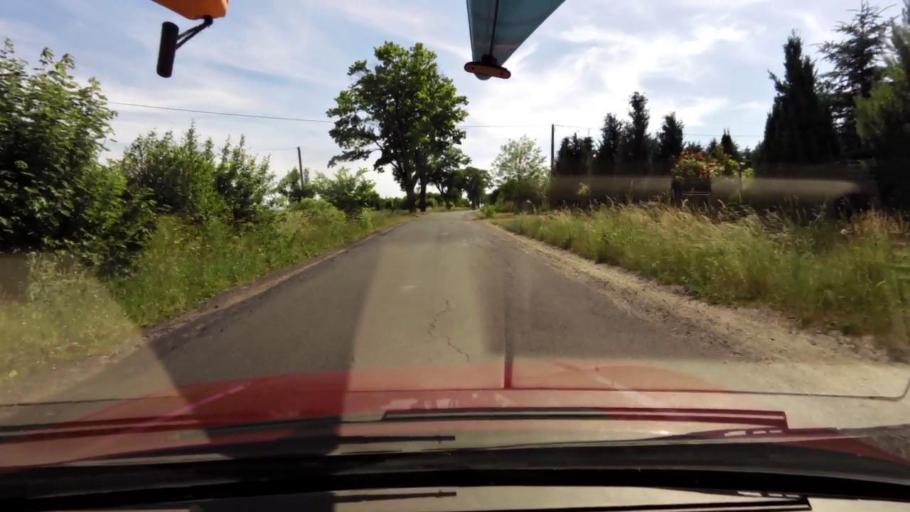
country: PL
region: Pomeranian Voivodeship
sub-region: Powiat slupski
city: Kobylnica
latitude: 54.4074
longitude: 17.0025
